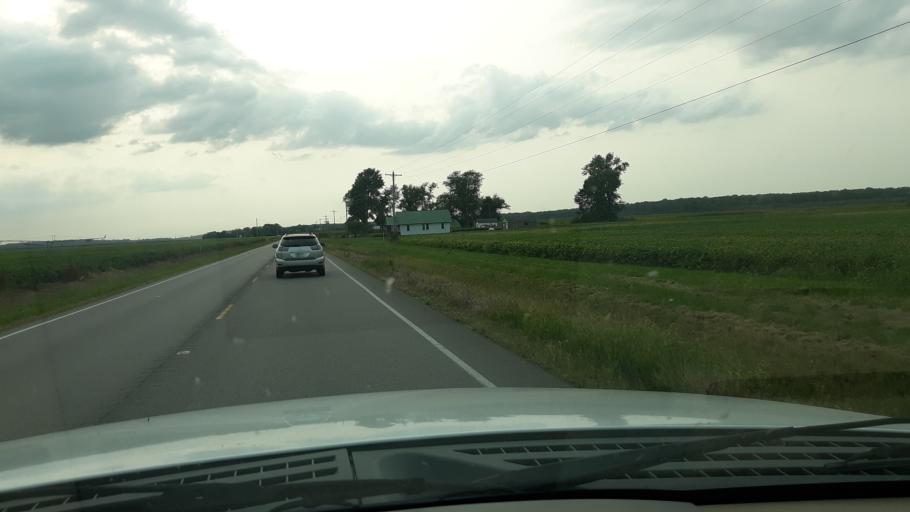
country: US
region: Indiana
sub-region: Gibson County
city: Owensville
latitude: 38.3559
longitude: -87.6753
